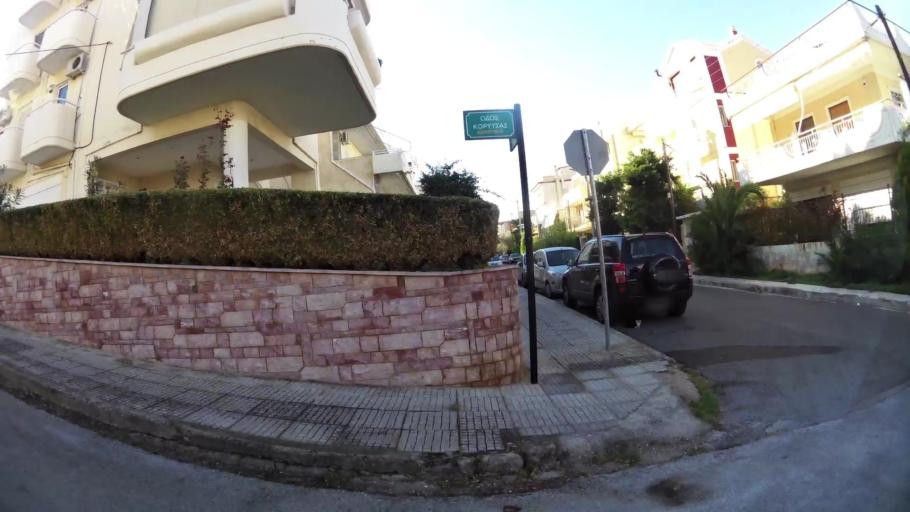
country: GR
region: Attica
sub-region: Nomarchia Athinas
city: Glyfada
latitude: 37.8764
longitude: 23.7703
